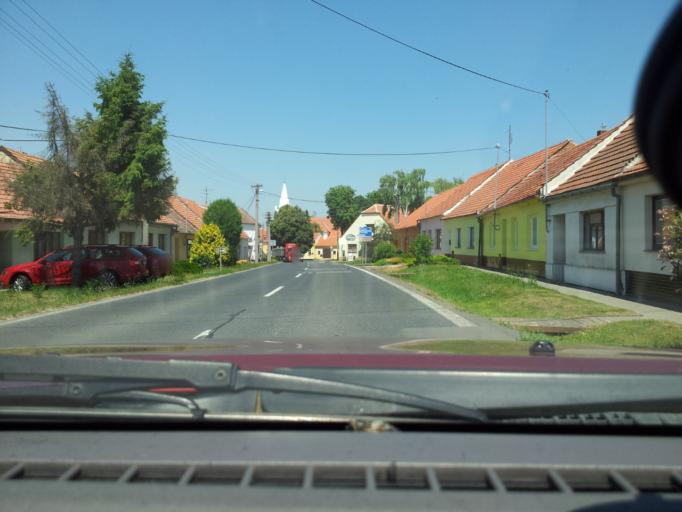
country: CZ
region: South Moravian
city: Telnice
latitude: 49.1002
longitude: 16.7179
